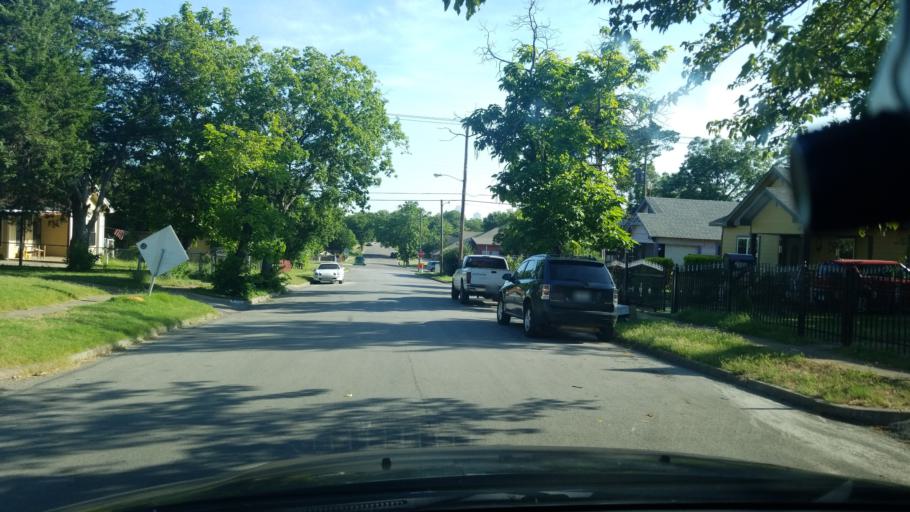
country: US
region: Texas
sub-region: Dallas County
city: Dallas
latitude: 32.7217
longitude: -96.8121
